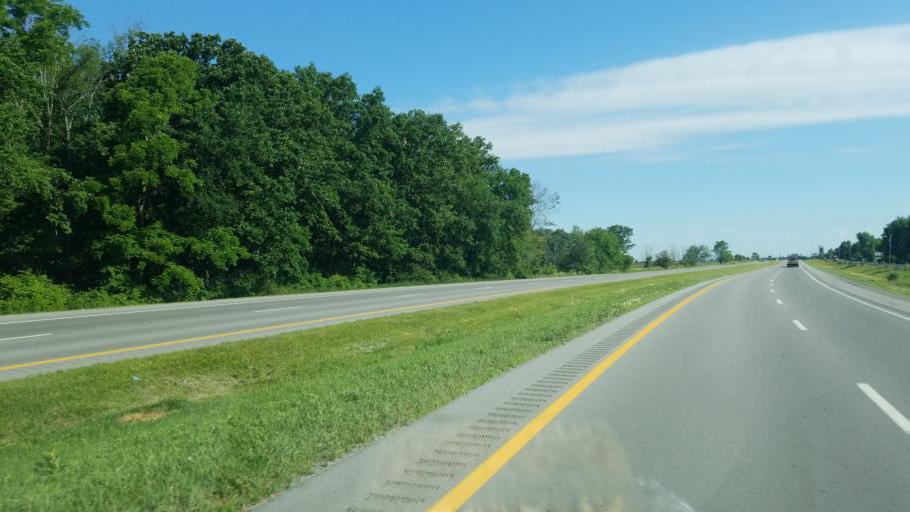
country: US
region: Ohio
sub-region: Hancock County
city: Findlay
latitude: 41.0047
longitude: -83.6604
